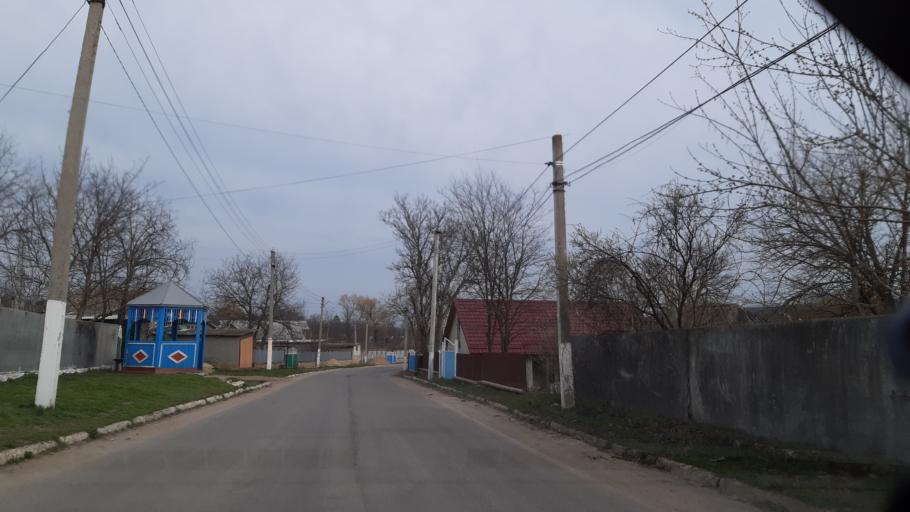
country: MD
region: Soldanesti
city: Soldanesti
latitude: 47.6851
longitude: 28.7566
